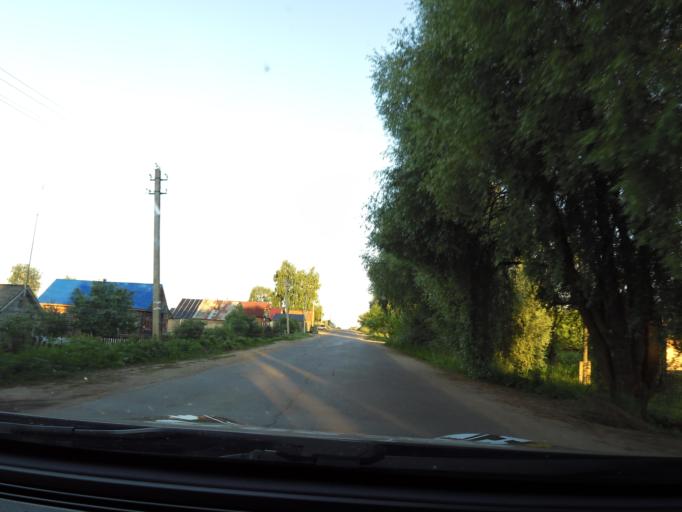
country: RU
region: Jaroslavl
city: Prechistoye
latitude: 58.4158
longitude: 40.3497
